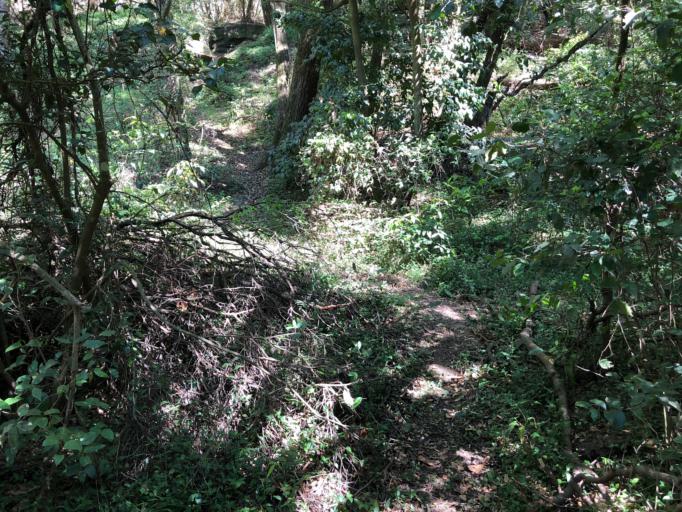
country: AU
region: New South Wales
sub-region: Hawkesbury
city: Scheyville
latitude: -33.5609
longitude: 150.9277
